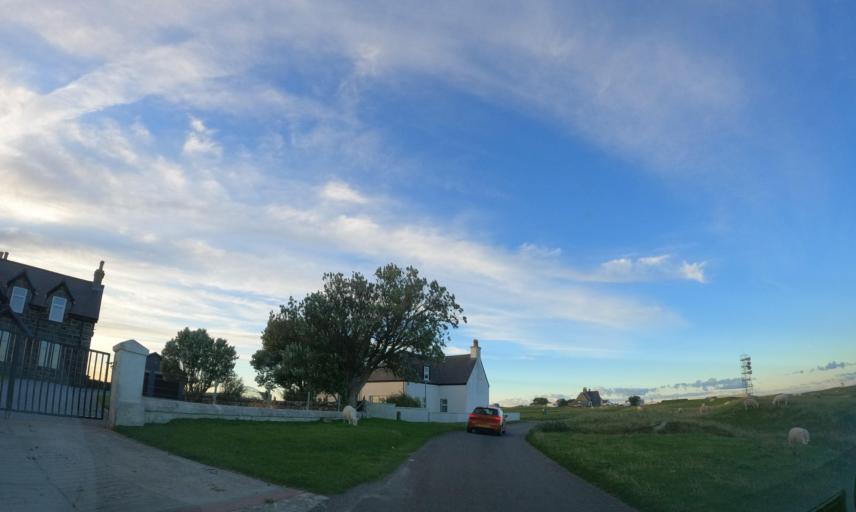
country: GB
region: Scotland
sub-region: Eilean Siar
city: Barra
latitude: 56.4979
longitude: -6.8104
